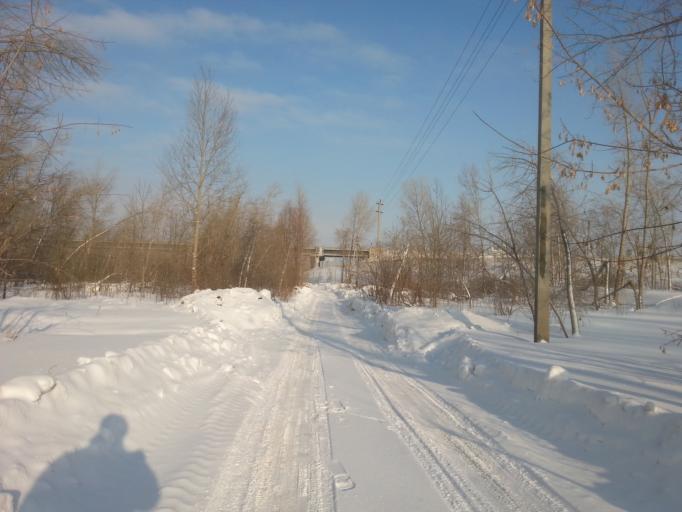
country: RU
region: Altai Krai
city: Zaton
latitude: 53.3185
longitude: 83.8086
